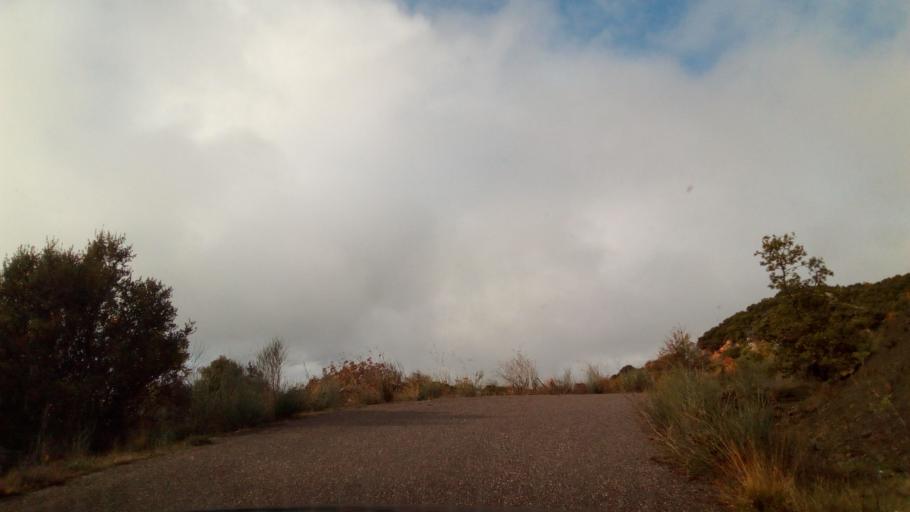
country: GR
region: West Greece
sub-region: Nomos Aitolias kai Akarnanias
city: Nafpaktos
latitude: 38.5183
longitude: 21.9518
